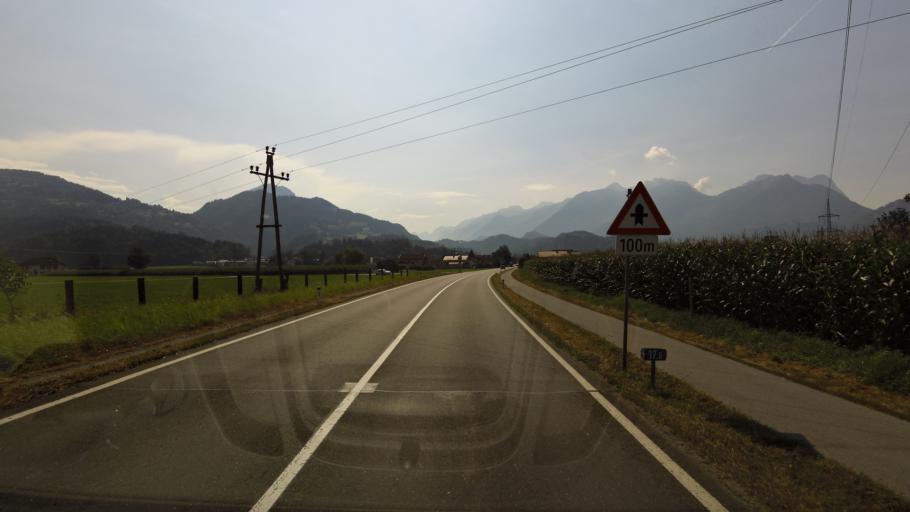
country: AT
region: Salzburg
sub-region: Politischer Bezirk Hallein
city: Kuchl
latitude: 47.6200
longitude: 13.1566
